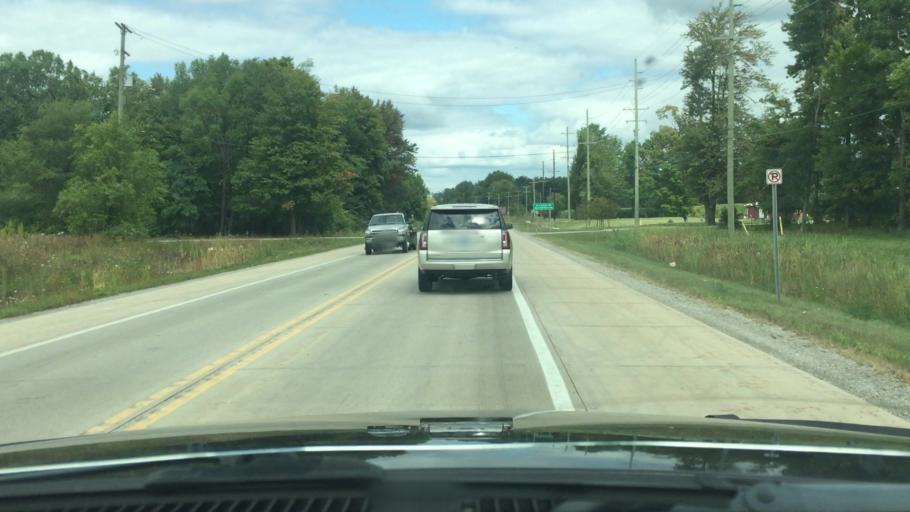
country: US
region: Michigan
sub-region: Lapeer County
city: Almont
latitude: 42.8648
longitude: -83.0215
